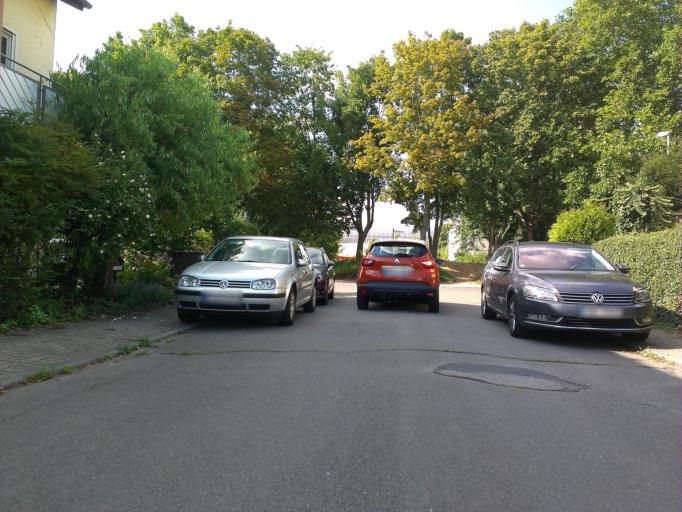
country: DE
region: Baden-Wuerttemberg
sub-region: Karlsruhe Region
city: Schriesheim
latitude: 49.4705
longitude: 8.6546
